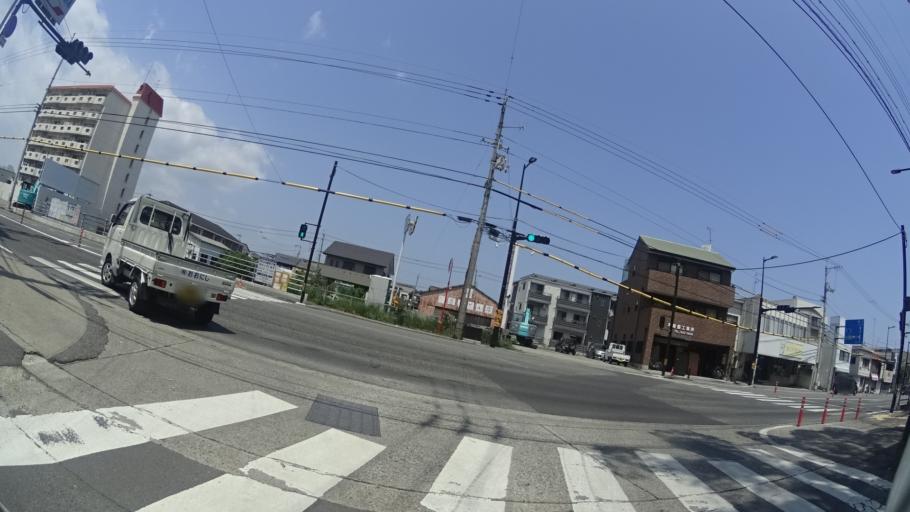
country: JP
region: Tokushima
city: Tokushima-shi
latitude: 34.0749
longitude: 134.5124
